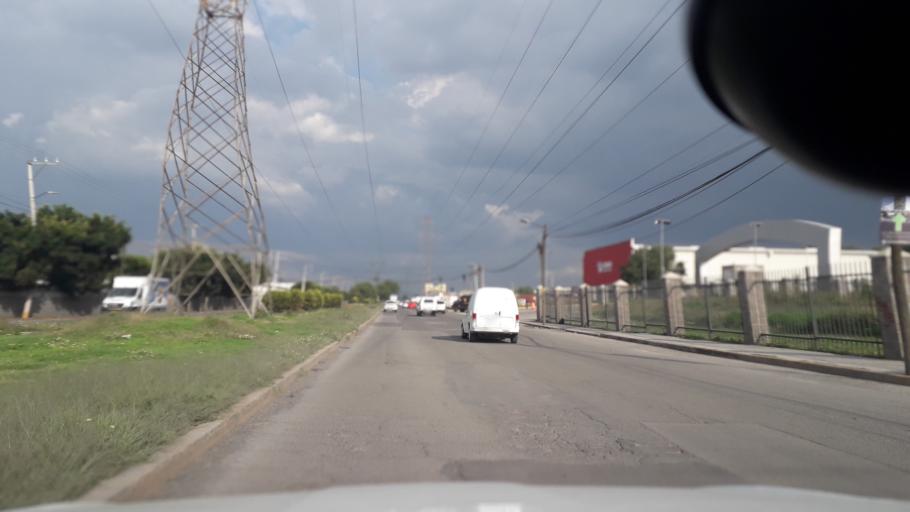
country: MX
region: Mexico
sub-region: Tultitlan
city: Colonia Lazaro Cardenas (Los Hornos)
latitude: 19.6396
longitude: -99.1467
